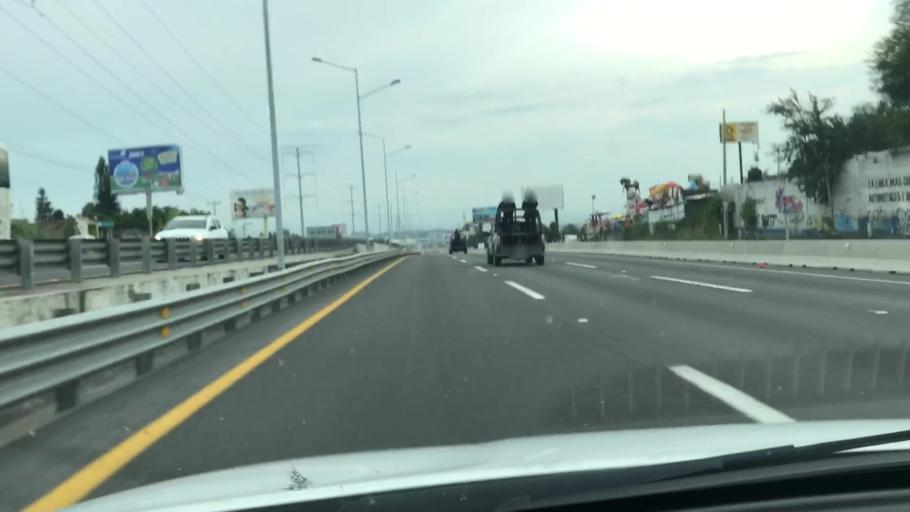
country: MX
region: Jalisco
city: Tonala
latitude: 20.6163
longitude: -103.2477
